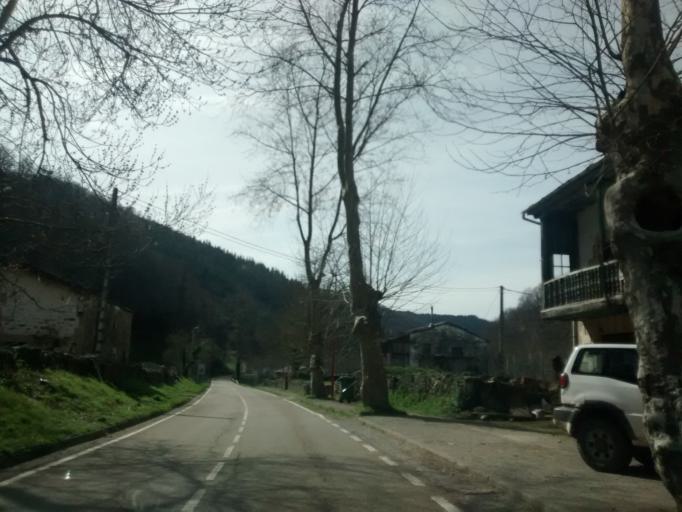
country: ES
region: Cantabria
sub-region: Provincia de Cantabria
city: Vega de Pas
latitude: 43.1579
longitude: -3.8024
